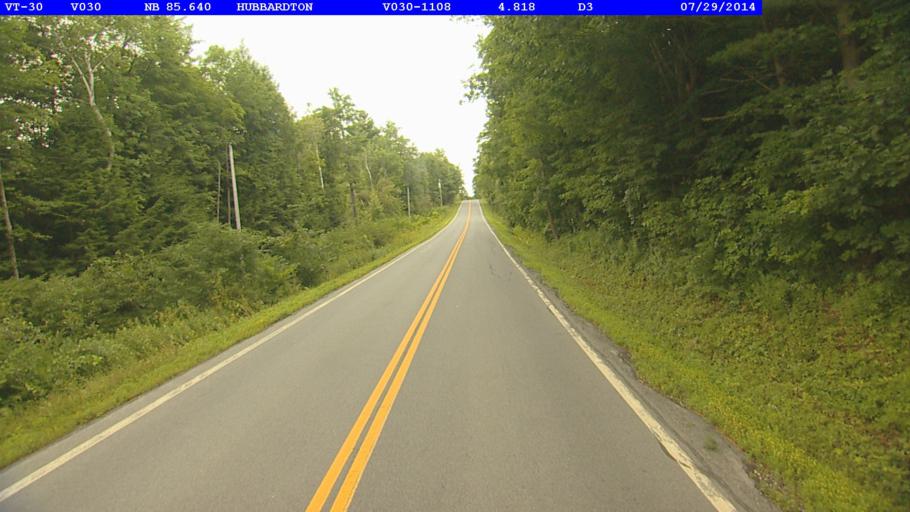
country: US
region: Vermont
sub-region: Rutland County
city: Brandon
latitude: 43.7456
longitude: -73.1870
